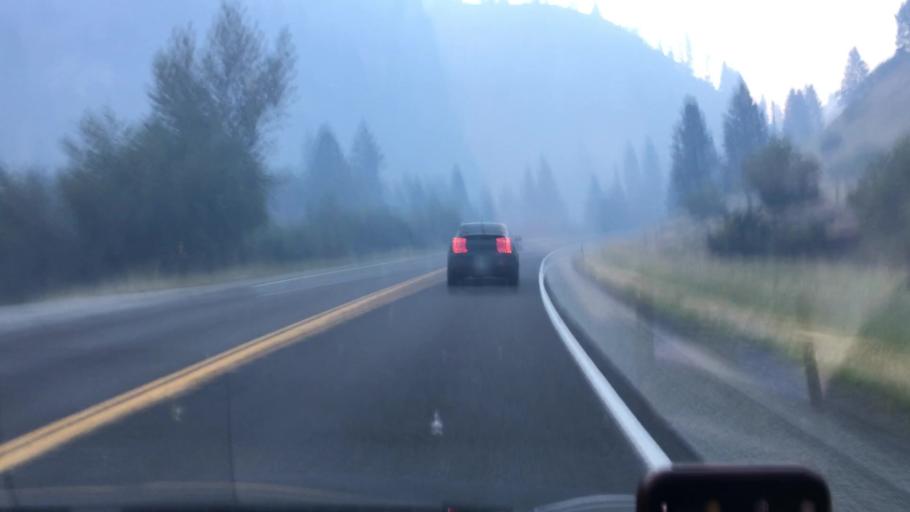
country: US
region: Idaho
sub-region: Valley County
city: McCall
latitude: 45.2710
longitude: -116.3462
